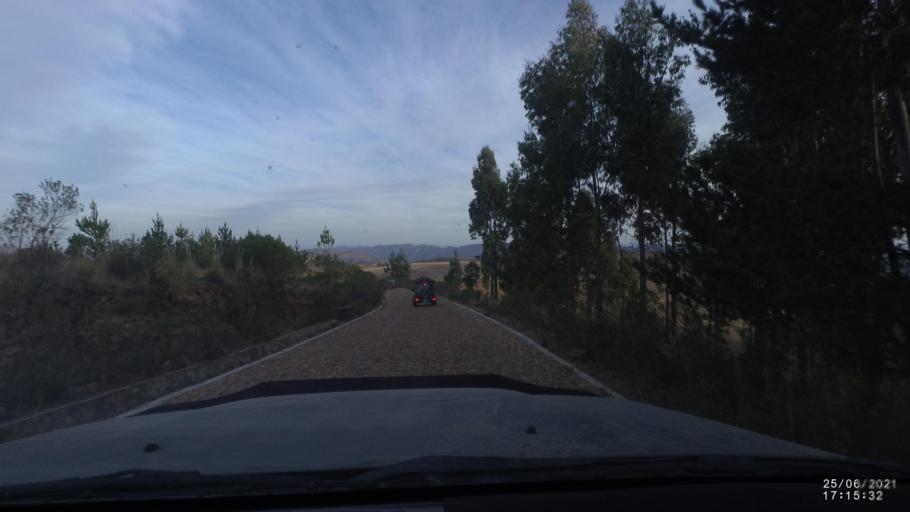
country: BO
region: Cochabamba
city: Arani
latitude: -17.8743
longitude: -65.6991
